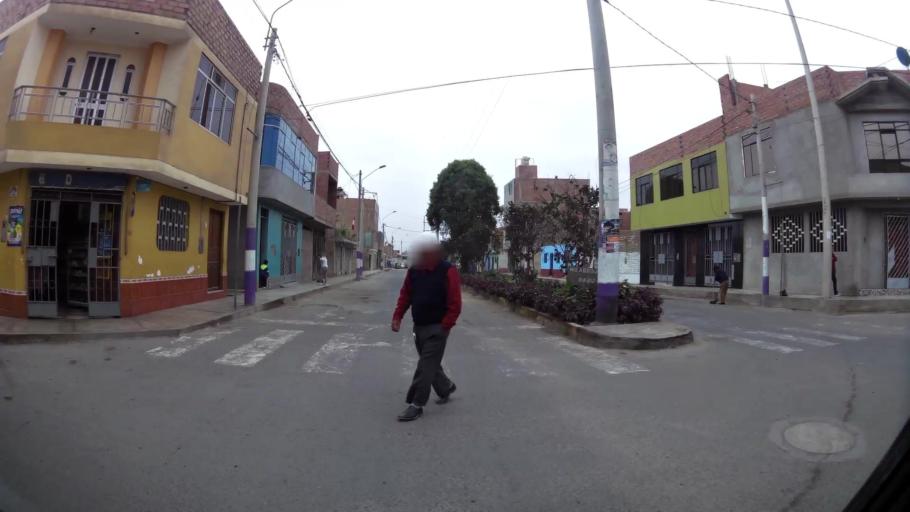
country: PE
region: Lima
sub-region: Barranca
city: Barranca
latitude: -10.7476
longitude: -77.7564
